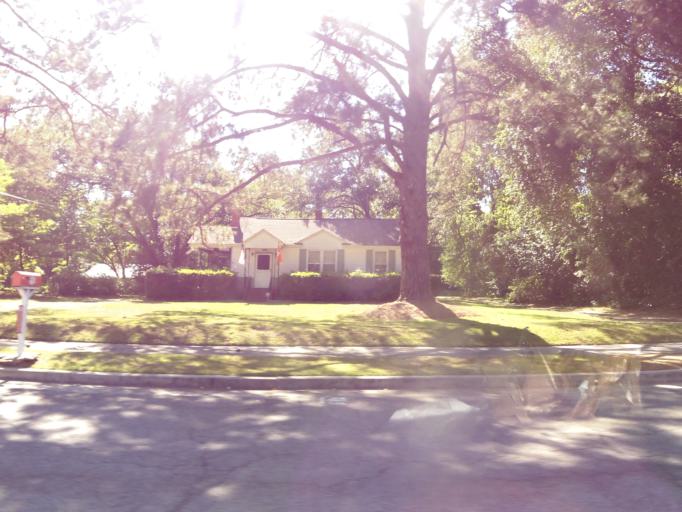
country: US
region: South Carolina
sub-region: Bamberg County
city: Denmark
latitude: 33.3100
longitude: -81.1443
